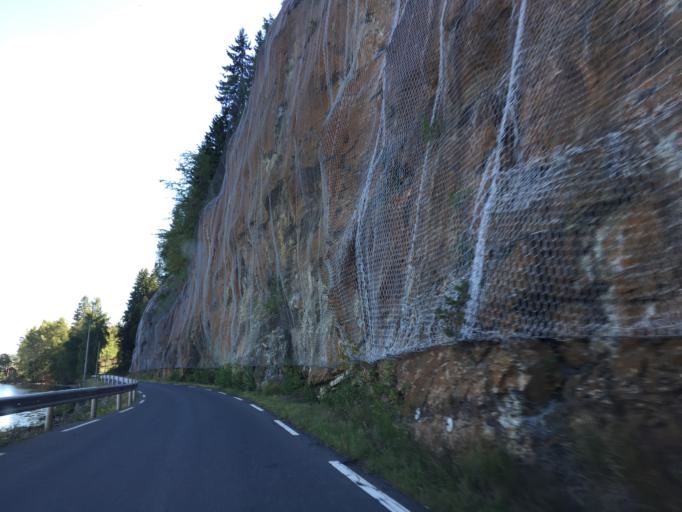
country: NO
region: Buskerud
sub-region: Ovre Eiker
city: Hokksund
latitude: 59.6794
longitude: 9.8617
